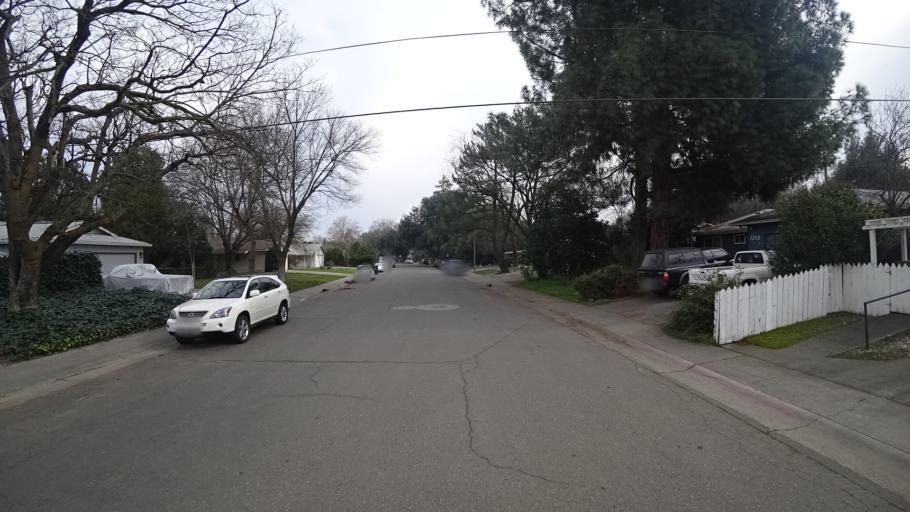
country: US
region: California
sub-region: Yolo County
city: Davis
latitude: 38.5552
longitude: -121.7346
